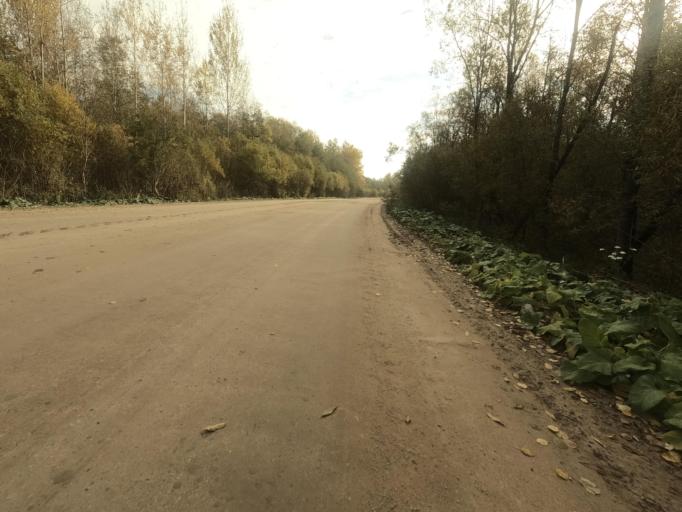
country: RU
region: Novgorod
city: Batetskiy
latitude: 58.8024
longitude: 30.6483
